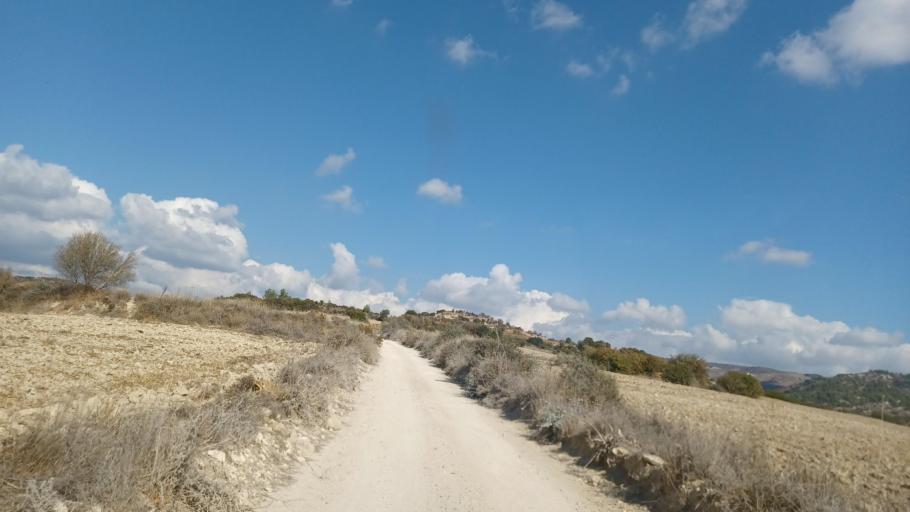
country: CY
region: Pafos
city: Mesogi
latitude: 34.8382
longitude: 32.5680
